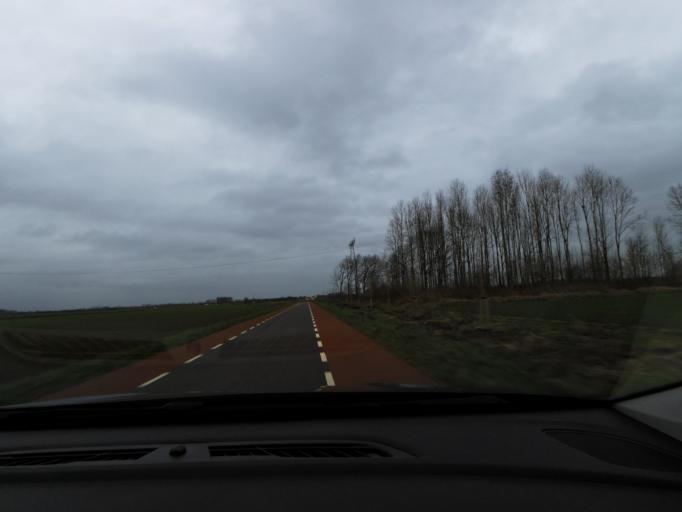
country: NL
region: North Brabant
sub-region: Gemeente Waalwijk
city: Waspik
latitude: 51.7078
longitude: 4.9840
